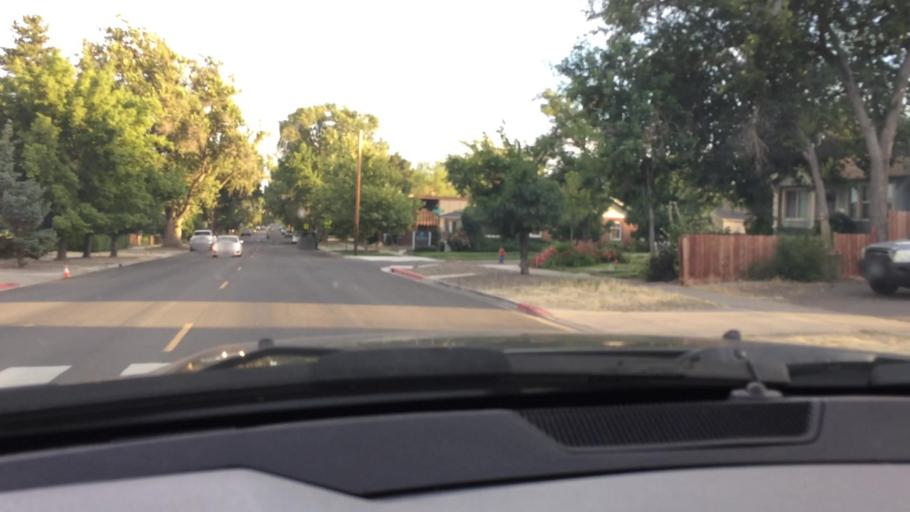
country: US
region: Nevada
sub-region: Washoe County
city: Reno
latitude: 39.5163
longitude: -119.8127
